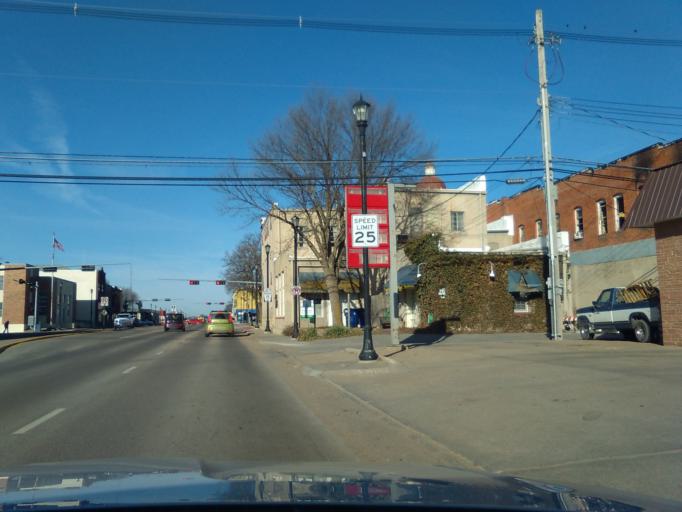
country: US
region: Nebraska
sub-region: Seward County
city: Seward
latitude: 40.9070
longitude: -97.0970
